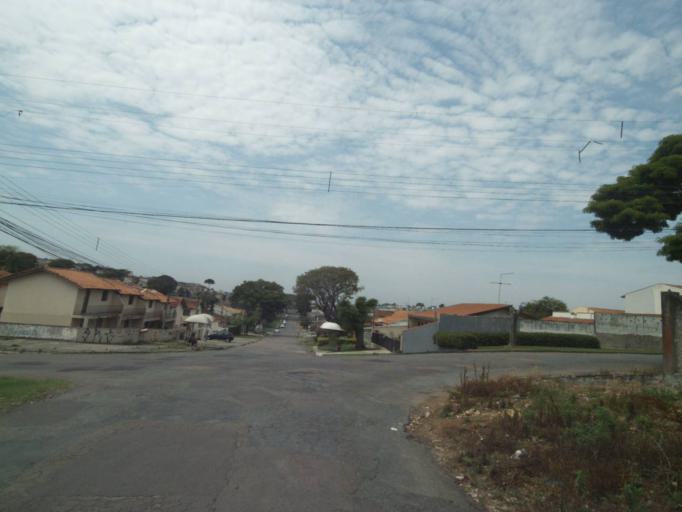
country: BR
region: Parana
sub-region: Pinhais
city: Pinhais
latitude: -25.3983
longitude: -49.2104
